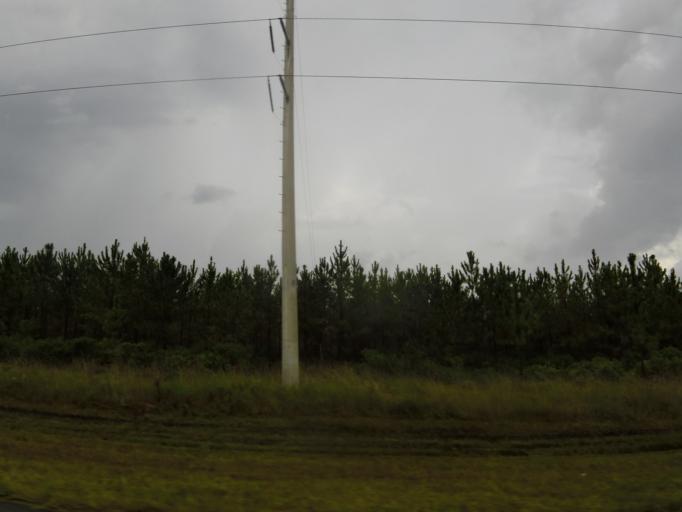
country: US
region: Florida
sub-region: Duval County
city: Baldwin
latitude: 30.4848
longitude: -82.0424
